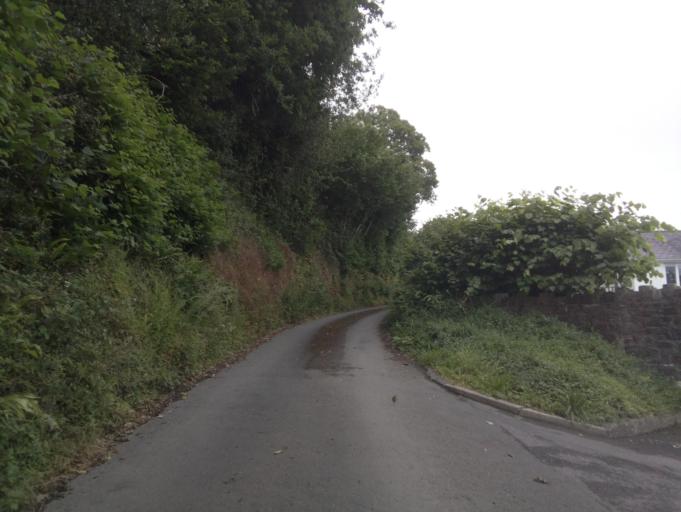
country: GB
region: England
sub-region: Devon
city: Ashburton
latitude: 50.5126
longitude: -3.7669
